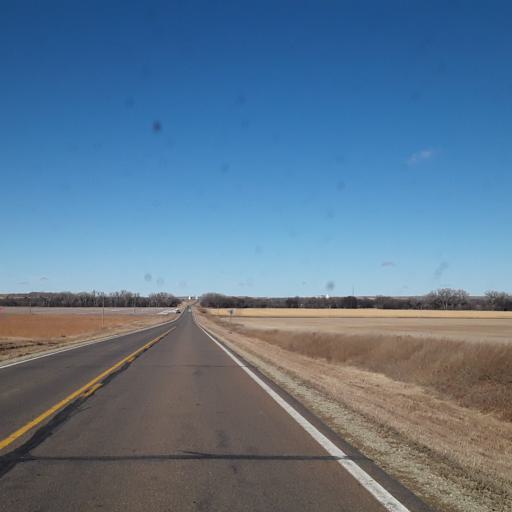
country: US
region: Kansas
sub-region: Lincoln County
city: Lincoln
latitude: 38.9965
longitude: -98.1513
